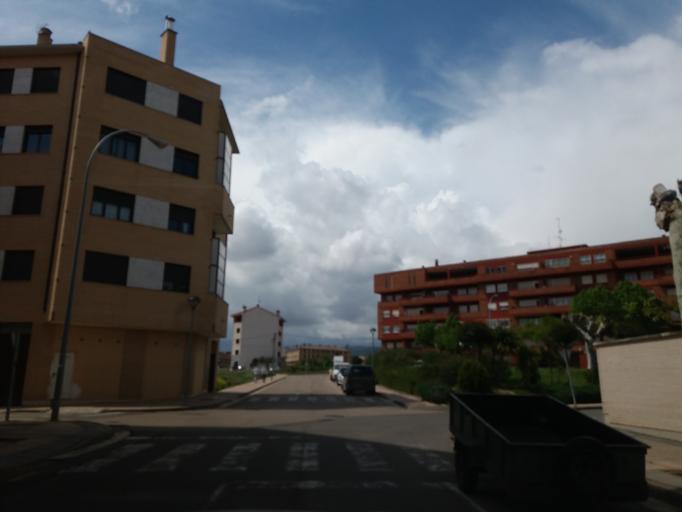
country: ES
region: La Rioja
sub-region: Provincia de La Rioja
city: Fuenmayor
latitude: 42.4681
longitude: -2.5634
